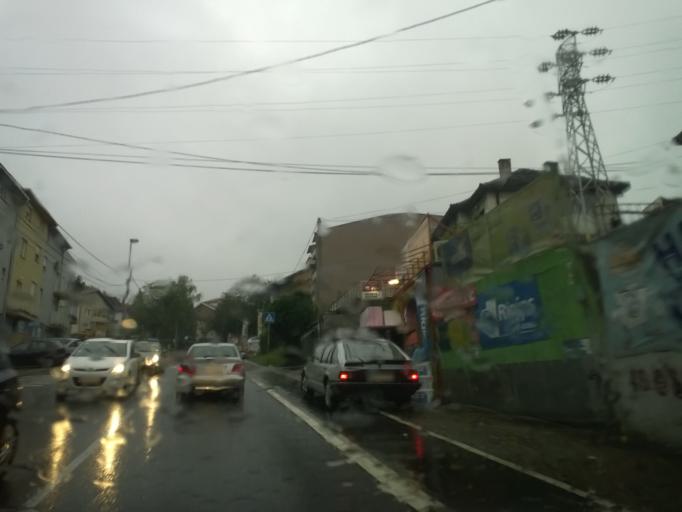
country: RS
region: Central Serbia
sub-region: Belgrade
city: Zvezdara
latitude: 44.7923
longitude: 20.5234
